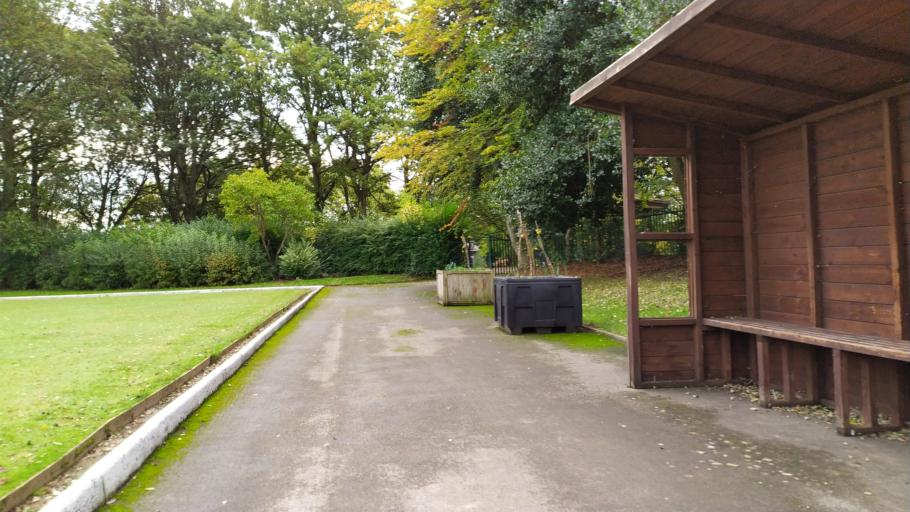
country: GB
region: England
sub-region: City and Borough of Leeds
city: Leeds
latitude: 53.8097
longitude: -1.5788
